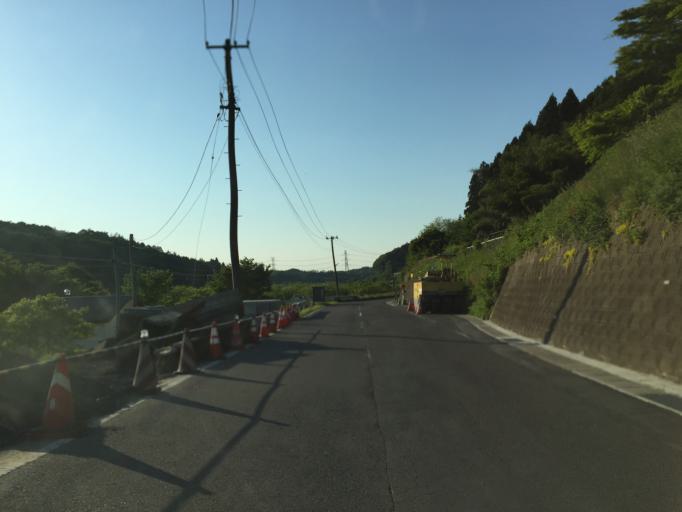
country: JP
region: Fukushima
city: Ishikawa
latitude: 37.0461
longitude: 140.4279
